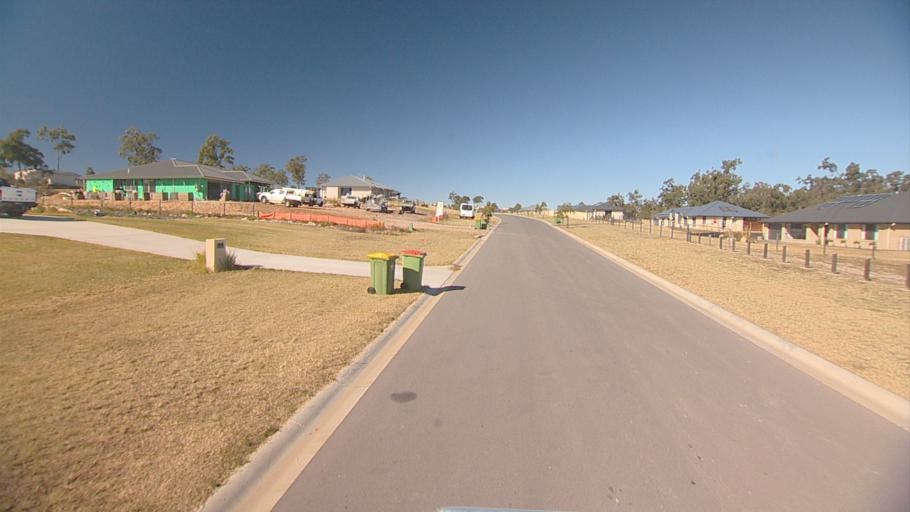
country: AU
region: Queensland
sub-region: Logan
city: North Maclean
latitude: -27.7481
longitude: 152.9424
